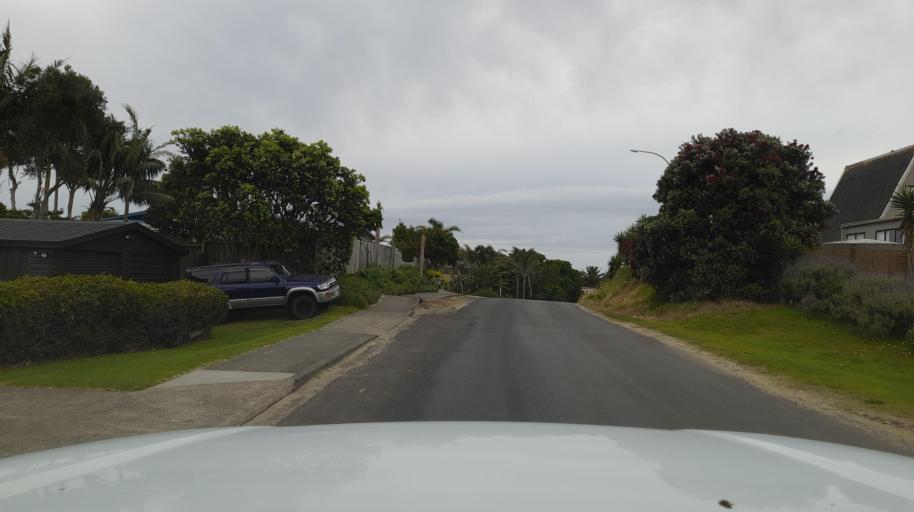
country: NZ
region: Northland
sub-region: Far North District
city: Ahipara
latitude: -35.1610
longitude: 173.1584
